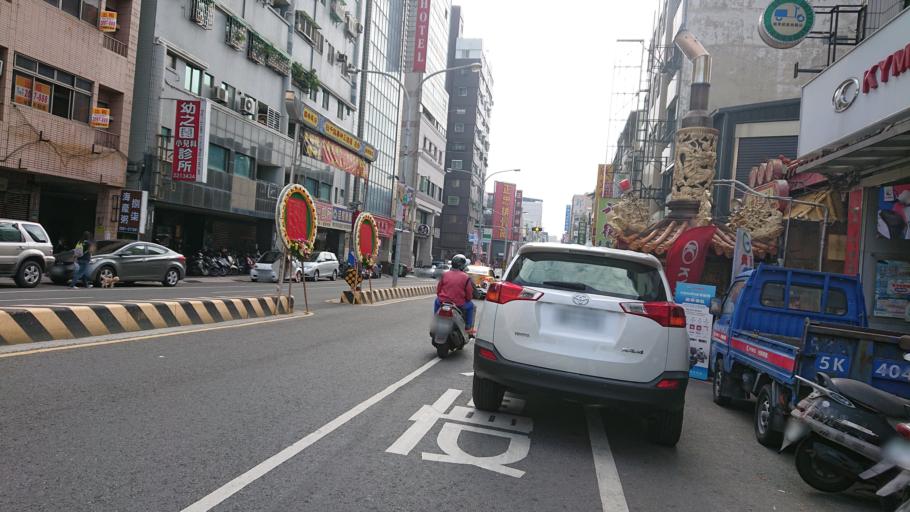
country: TW
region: Taiwan
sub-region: Tainan
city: Tainan
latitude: 22.9996
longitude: 120.2054
